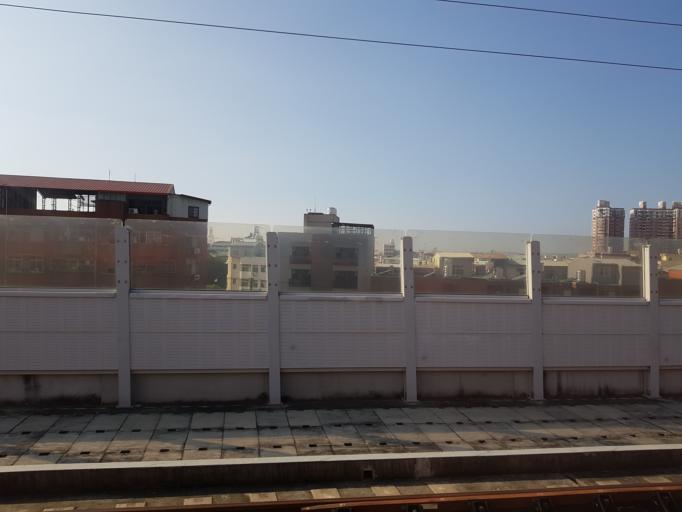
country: TW
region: Taiwan
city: Fengyuan
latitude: 24.2562
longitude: 120.7246
